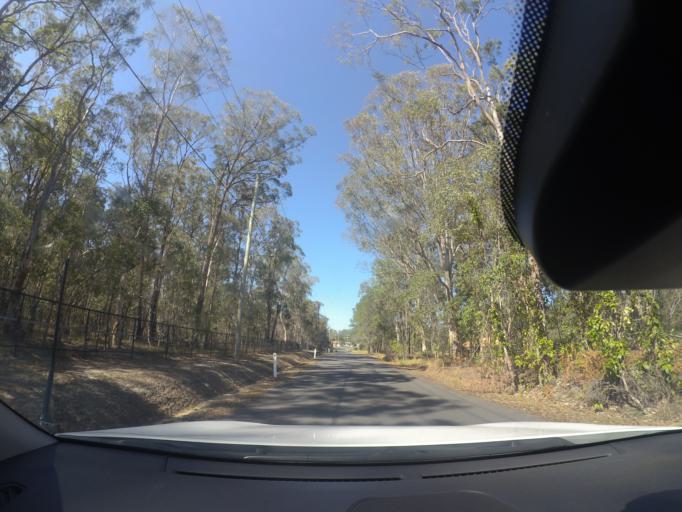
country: AU
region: Queensland
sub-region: Logan
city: Woodridge
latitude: -27.6407
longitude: 153.0938
